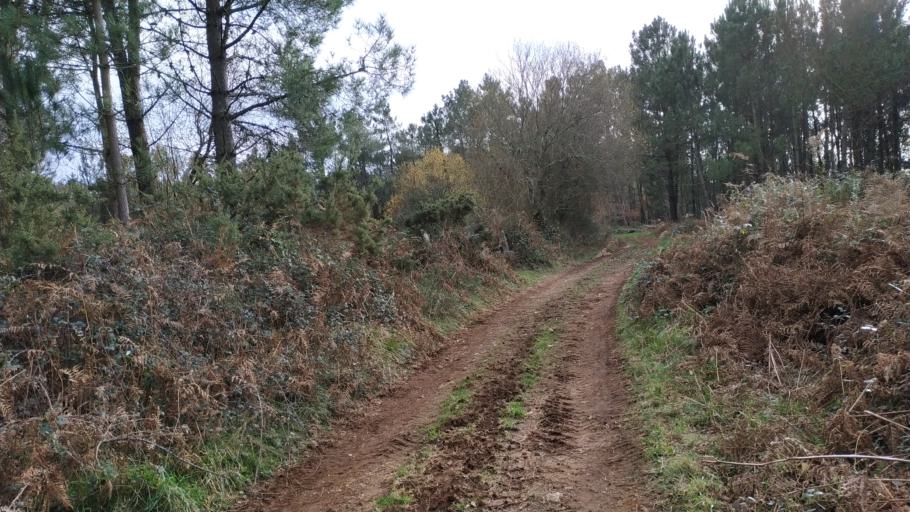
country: ES
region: Galicia
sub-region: Provincia de Pontevedra
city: Silleda
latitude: 42.7733
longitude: -8.1630
